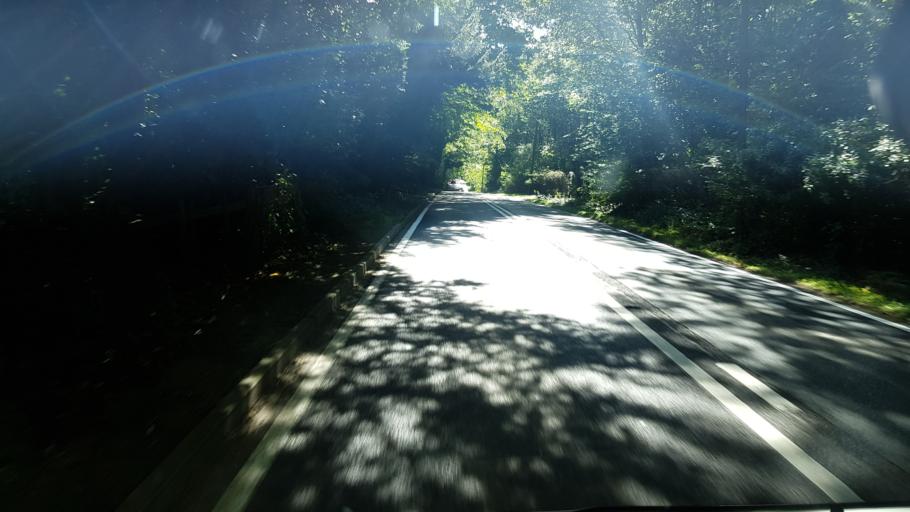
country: GB
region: England
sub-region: Kent
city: Kings Hill
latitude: 51.2772
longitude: 0.3541
